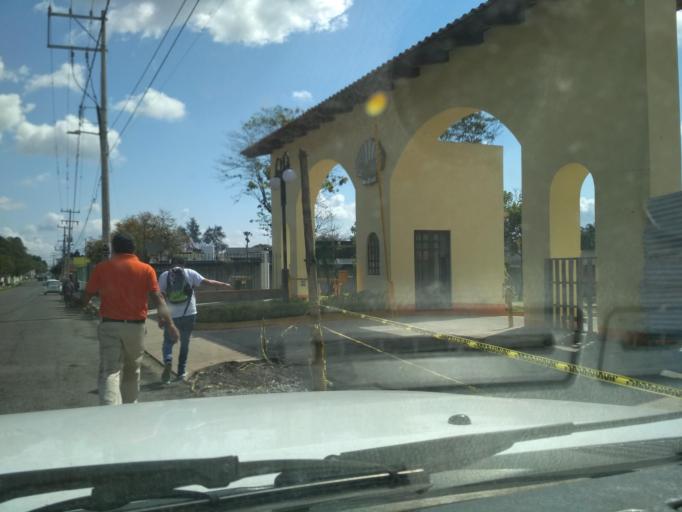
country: MX
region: Veracruz
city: Coatepec
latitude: 19.4510
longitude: -96.9480
